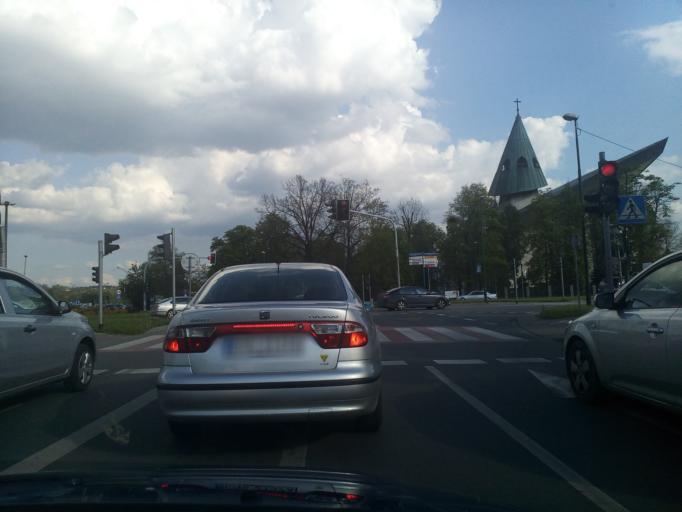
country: PL
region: Lesser Poland Voivodeship
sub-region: Powiat nowosadecki
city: Nowy Sacz
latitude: 49.6177
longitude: 20.7140
